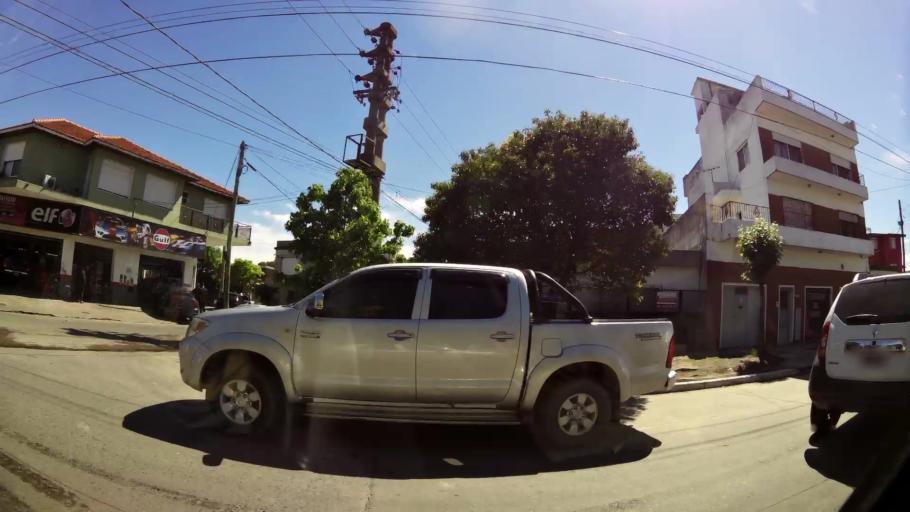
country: AR
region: Buenos Aires
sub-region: Partido de Quilmes
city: Quilmes
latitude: -34.7018
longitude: -58.2812
